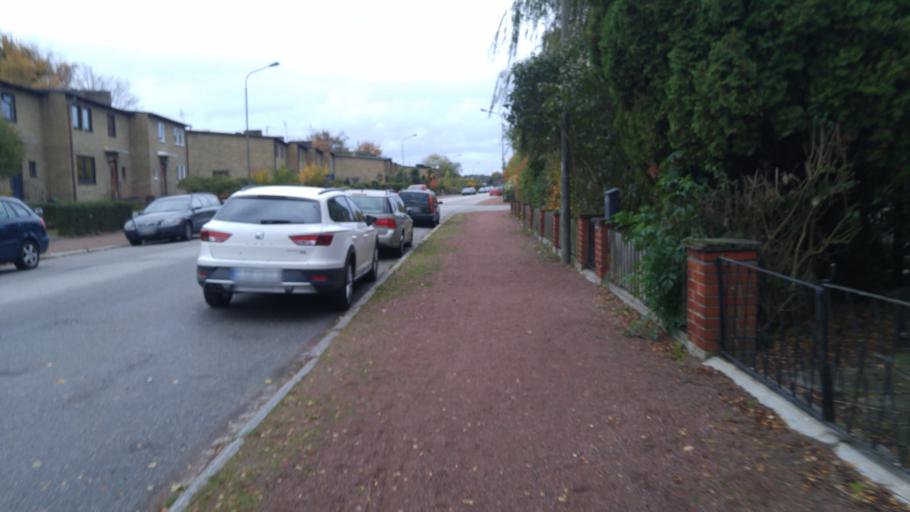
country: SE
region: Skane
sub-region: Malmo
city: Bunkeflostrand
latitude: 55.5776
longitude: 12.9519
